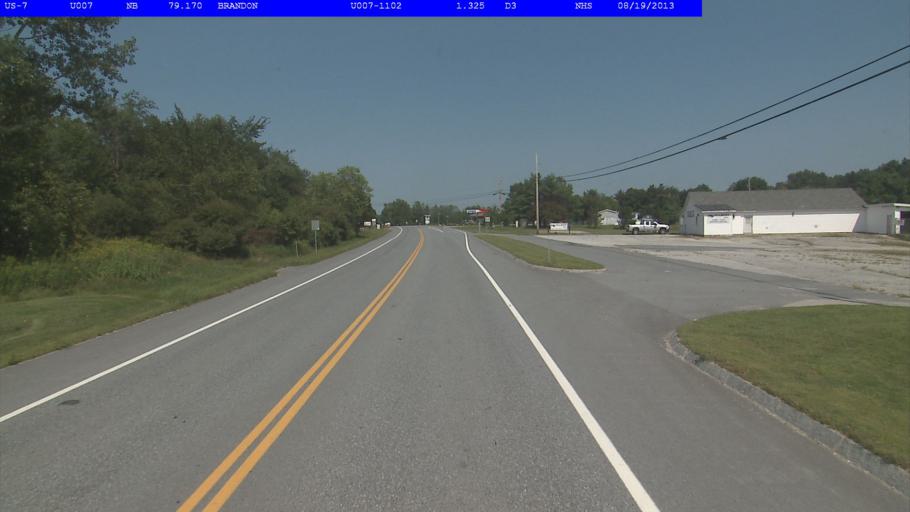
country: US
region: Vermont
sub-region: Rutland County
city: Brandon
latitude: 43.7731
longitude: -73.0525
